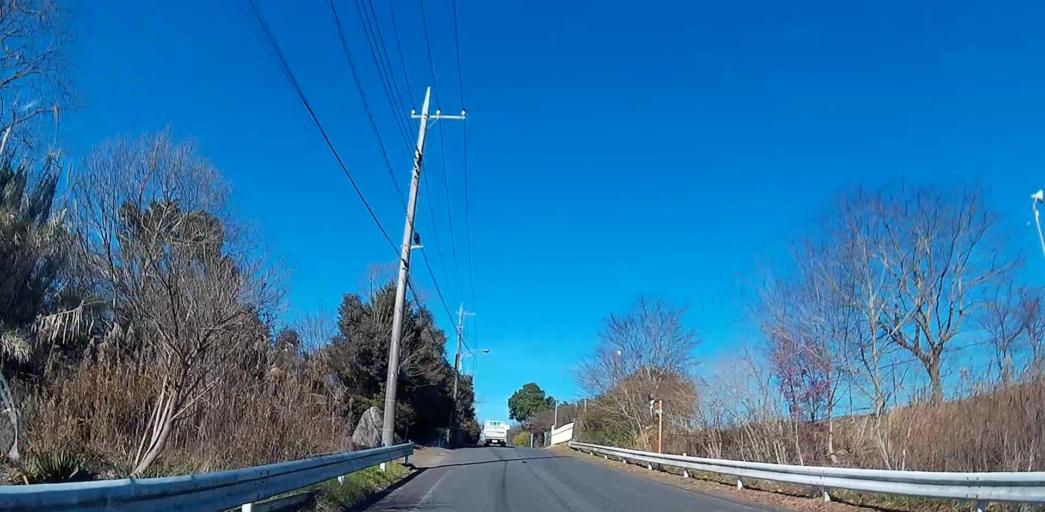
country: JP
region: Chiba
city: Narita
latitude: 35.7894
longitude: 140.3817
